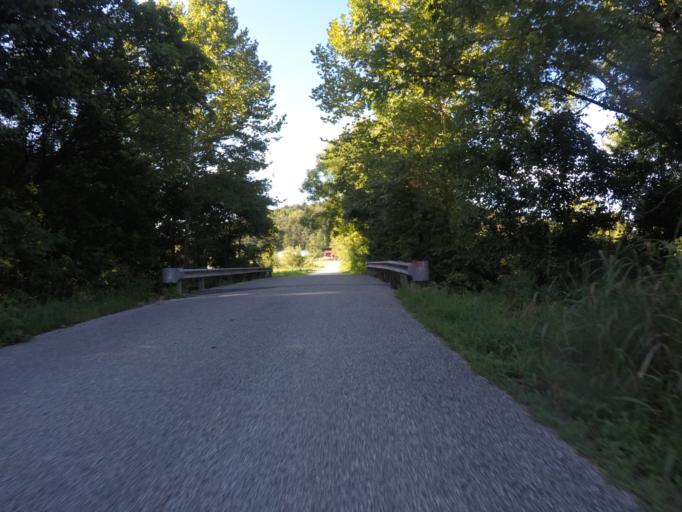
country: US
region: West Virginia
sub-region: Cabell County
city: Huntington
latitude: 38.5009
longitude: -82.4880
